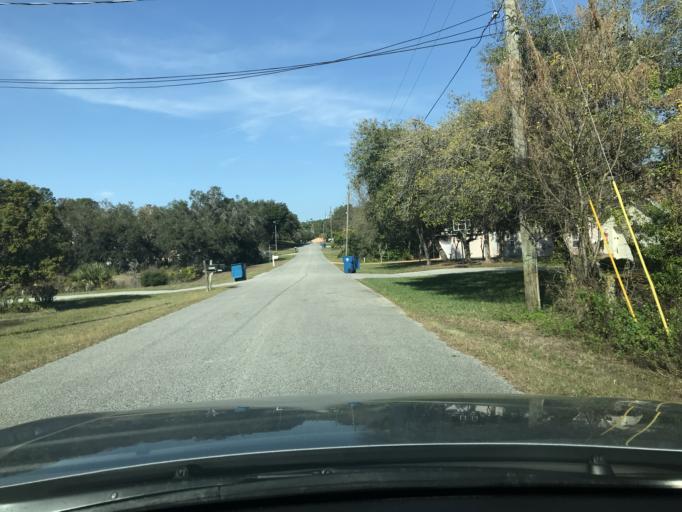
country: US
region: Florida
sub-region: Hernando County
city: North Weeki Wachee
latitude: 28.5518
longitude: -82.5463
